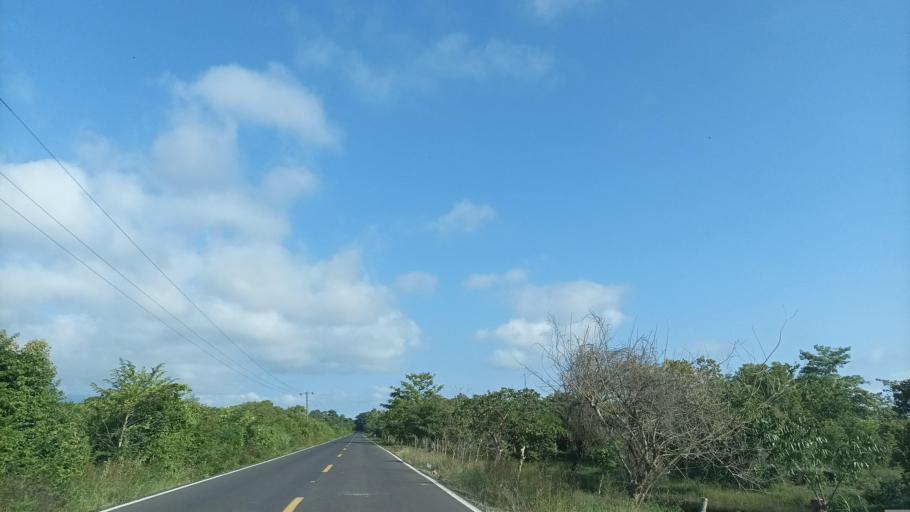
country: MX
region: Veracruz
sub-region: Chinameca
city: Chacalapa
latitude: 18.1599
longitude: -94.6576
